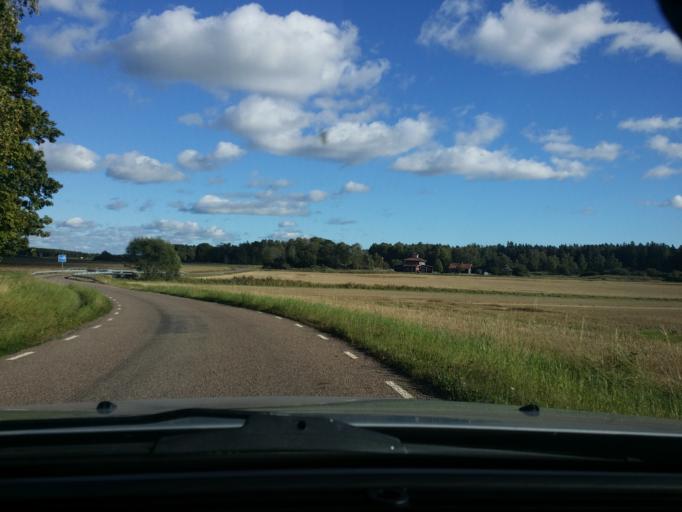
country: SE
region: Vaestmanland
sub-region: Vasteras
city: Vasteras
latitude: 59.5383
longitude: 16.4617
